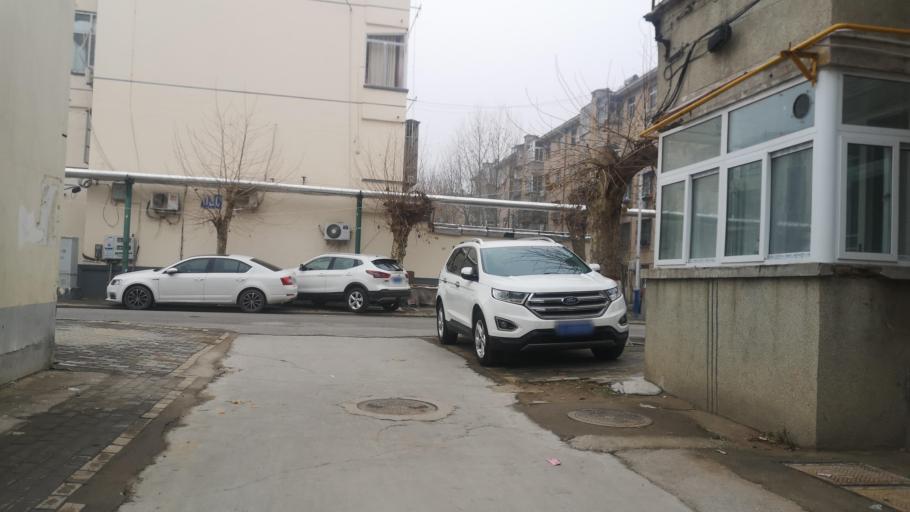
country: CN
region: Henan Sheng
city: Zhongyuanlu
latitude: 35.7647
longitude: 115.0696
